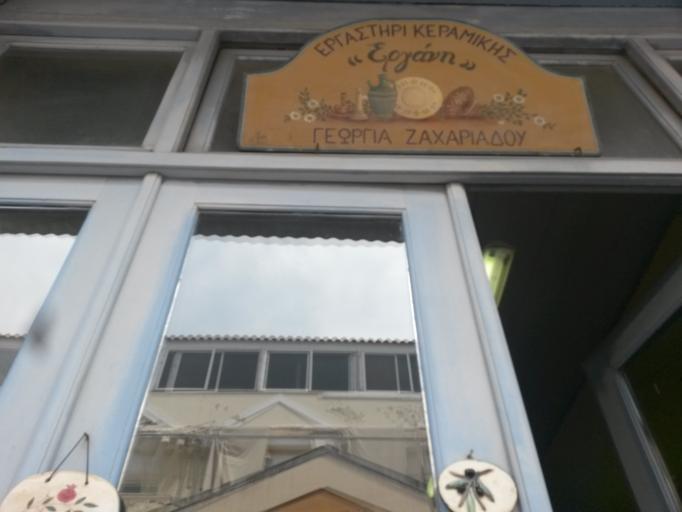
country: GR
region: North Aegean
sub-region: Nomos Lesvou
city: Mytilini
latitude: 39.1106
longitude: 26.5575
